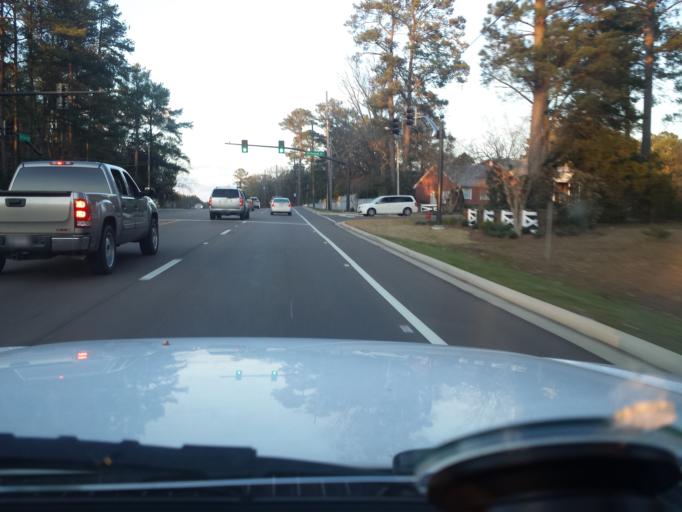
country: US
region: Mississippi
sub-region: Rankin County
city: Flowood
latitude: 32.3622
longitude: -90.0567
